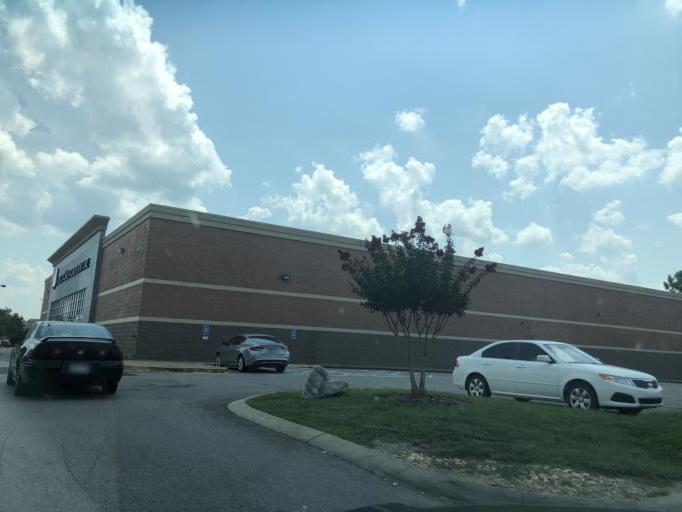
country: US
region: Tennessee
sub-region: Rutherford County
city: Murfreesboro
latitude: 35.8460
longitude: -86.4286
